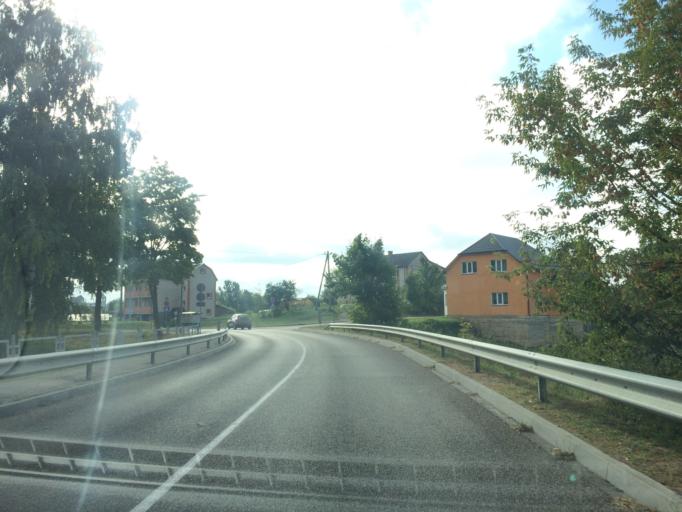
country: LV
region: Rezekne
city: Rezekne
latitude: 56.4921
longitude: 27.3282
